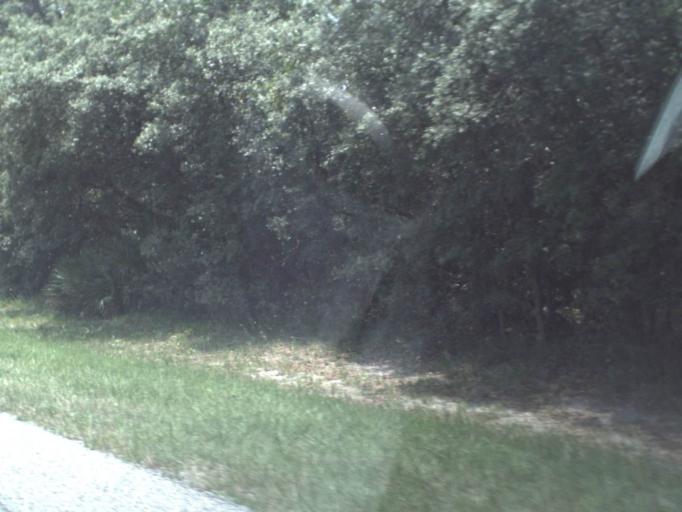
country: US
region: Florida
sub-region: Saint Johns County
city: Butler Beach
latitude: 29.6766
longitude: -81.2920
